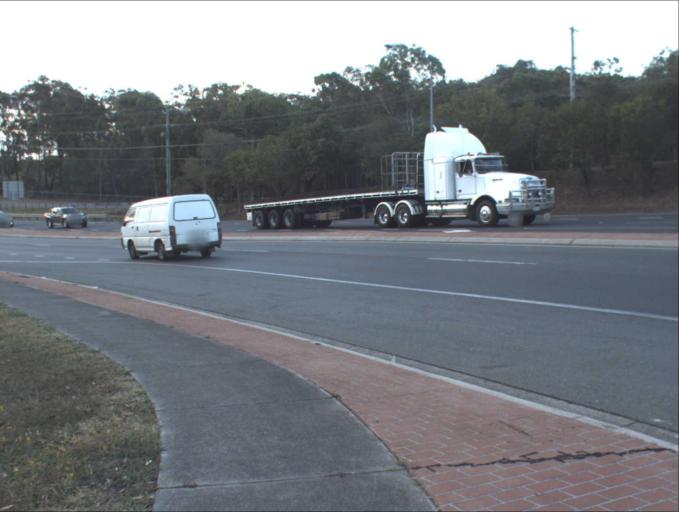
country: AU
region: Queensland
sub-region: Logan
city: Beenleigh
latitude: -27.6705
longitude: 153.2021
